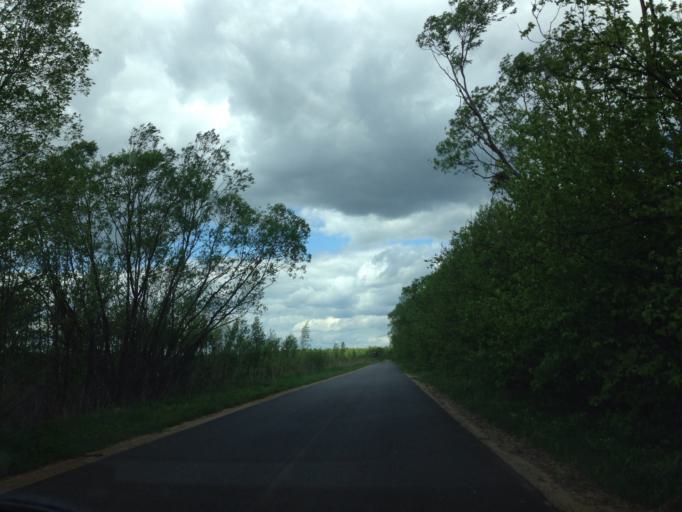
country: PL
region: Podlasie
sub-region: Powiat bialostocki
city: Tykocin
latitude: 53.2939
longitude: 22.6073
